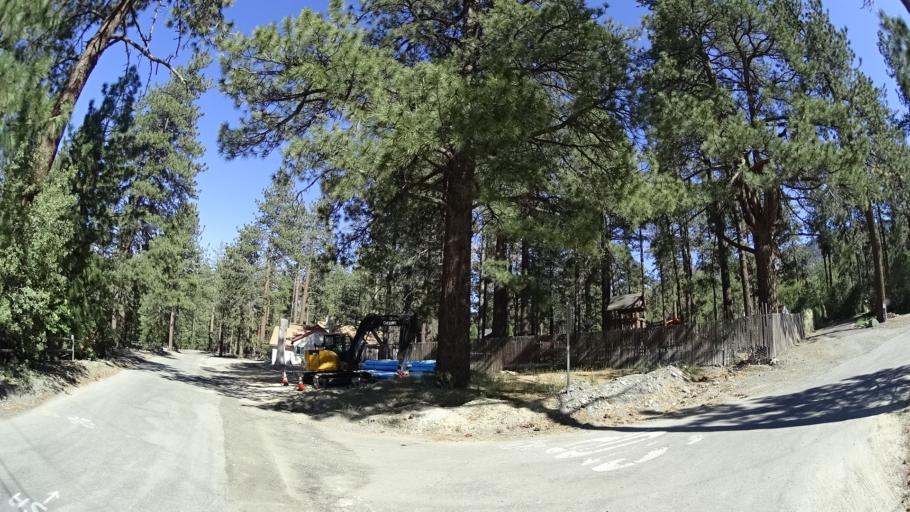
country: US
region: California
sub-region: San Bernardino County
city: Wrightwood
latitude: 34.3601
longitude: -117.6410
